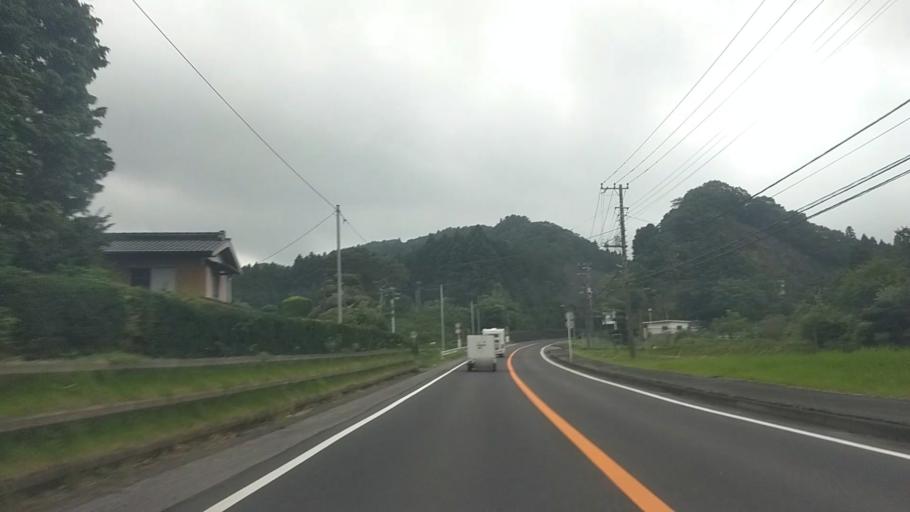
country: JP
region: Chiba
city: Kawaguchi
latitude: 35.1837
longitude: 140.0611
